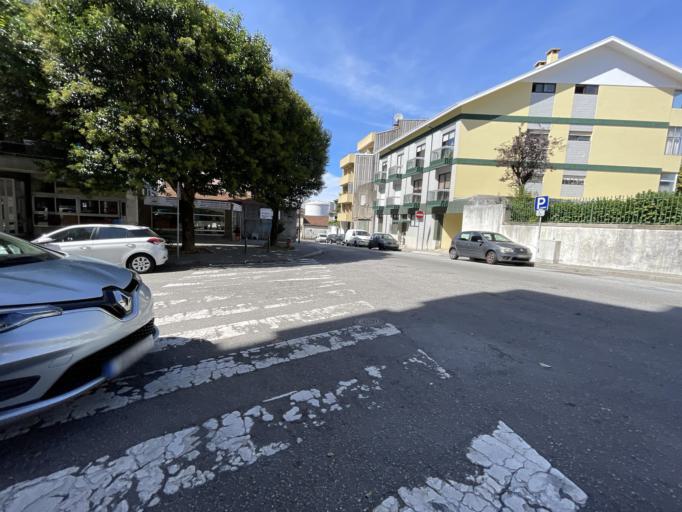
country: PT
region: Porto
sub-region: Vila Nova de Gaia
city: Vila Nova de Gaia
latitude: 41.1276
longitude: -8.6221
